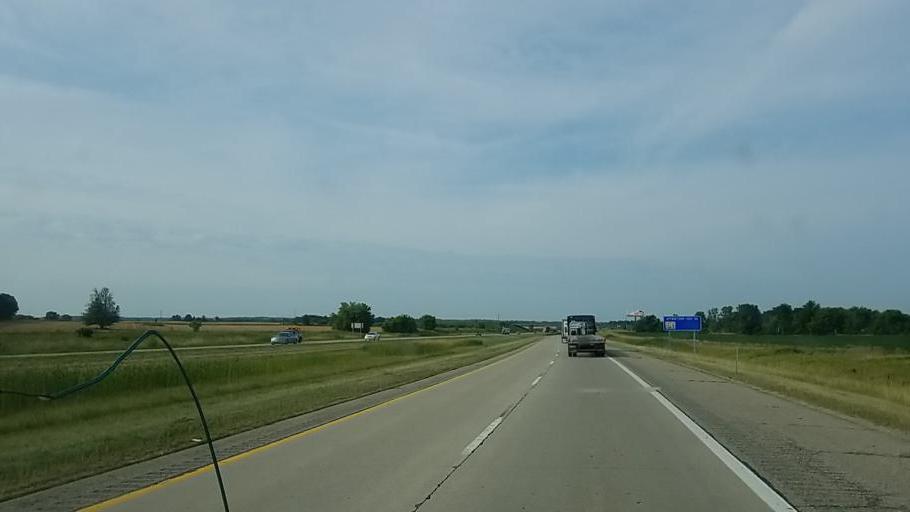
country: US
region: Michigan
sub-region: Eaton County
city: Potterville
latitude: 42.6307
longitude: -84.7254
